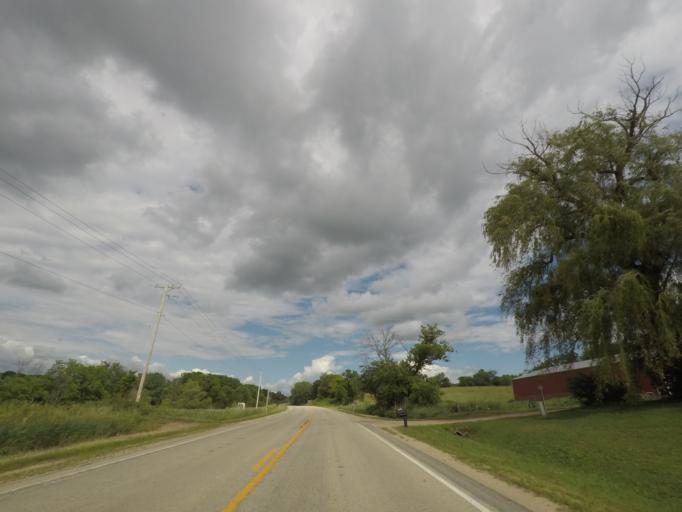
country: US
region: Wisconsin
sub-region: Green County
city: Brooklyn
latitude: 42.8271
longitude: -89.4335
